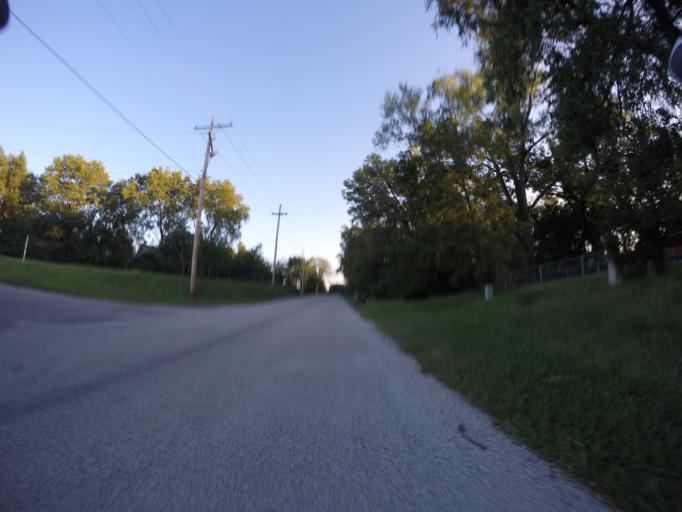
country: US
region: Kansas
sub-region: Riley County
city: Ogden
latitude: 39.1188
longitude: -96.7114
